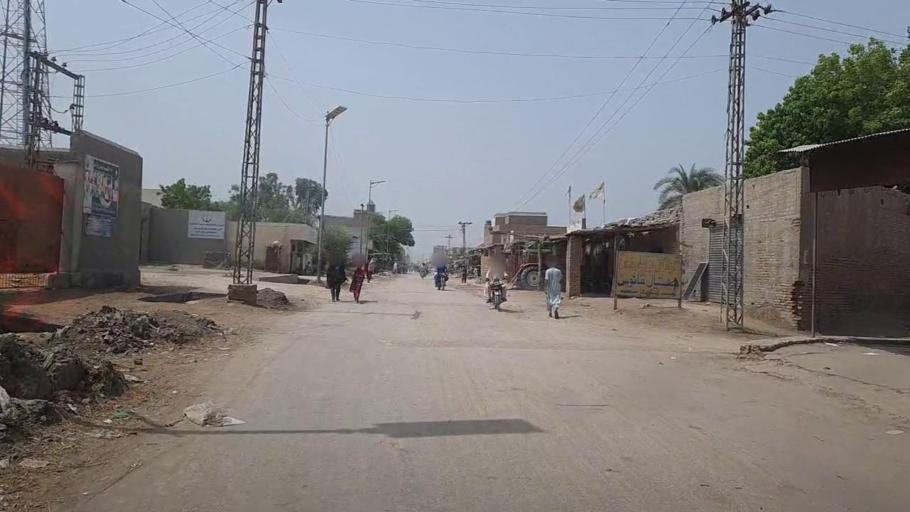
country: PK
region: Sindh
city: Radhan
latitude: 27.1755
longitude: 67.9486
